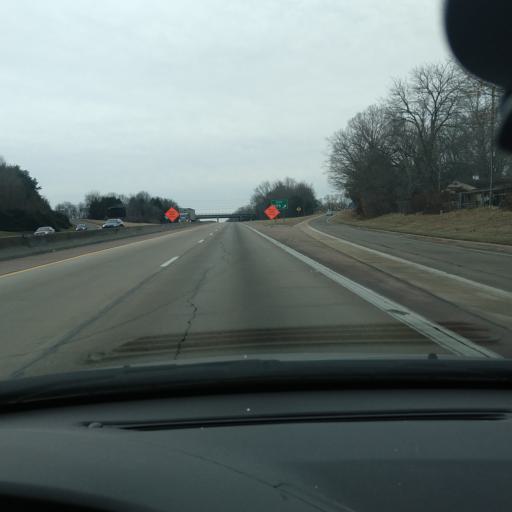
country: US
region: North Carolina
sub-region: Forsyth County
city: Winston-Salem
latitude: 36.0505
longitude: -80.2355
